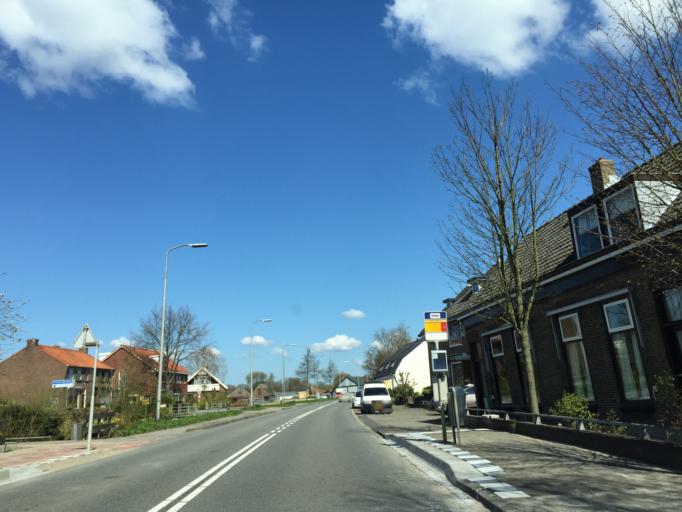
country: NL
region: South Holland
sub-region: Gemeente Pijnacker-Nootdorp
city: Pijnacker
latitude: 52.0249
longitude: 4.4354
